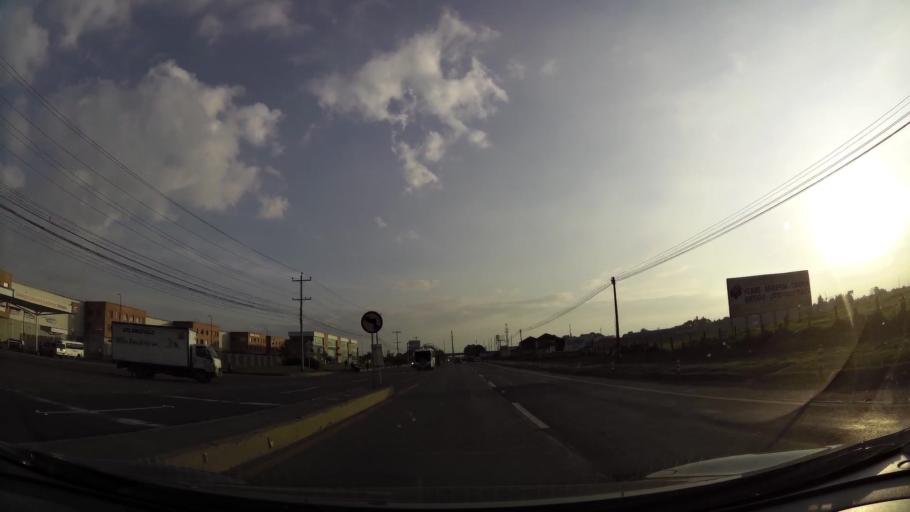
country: CO
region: Cundinamarca
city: Cota
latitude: 4.7619
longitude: -74.1541
